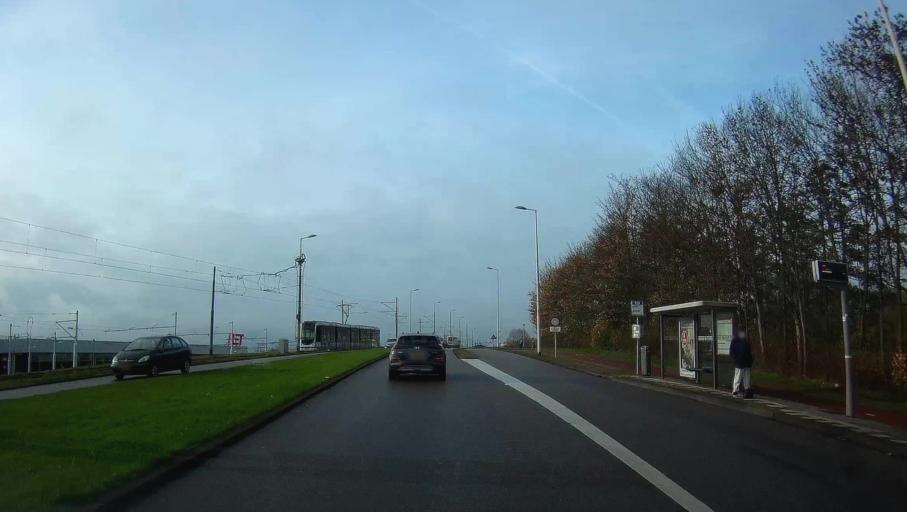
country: NL
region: South Holland
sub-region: Gemeente Capelle aan den IJssel
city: Capelle-West
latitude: 51.8859
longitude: 4.5670
